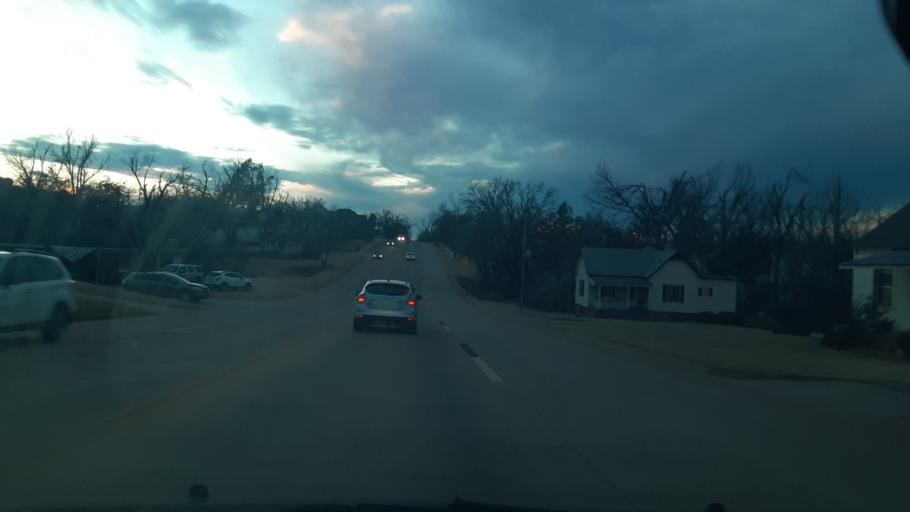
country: US
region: Oklahoma
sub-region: Logan County
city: Guthrie
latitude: 35.8802
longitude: -97.4093
